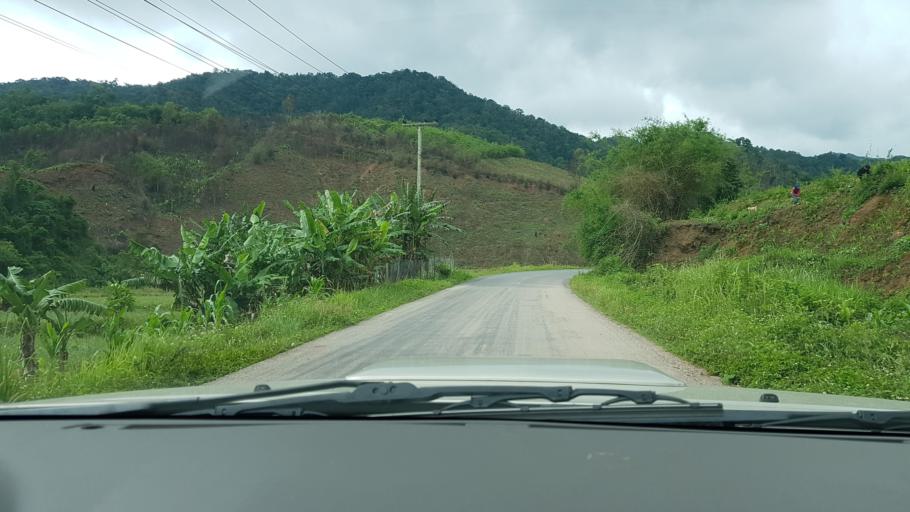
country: LA
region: Oudomxai
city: Muang Xay
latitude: 20.5597
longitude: 101.9143
